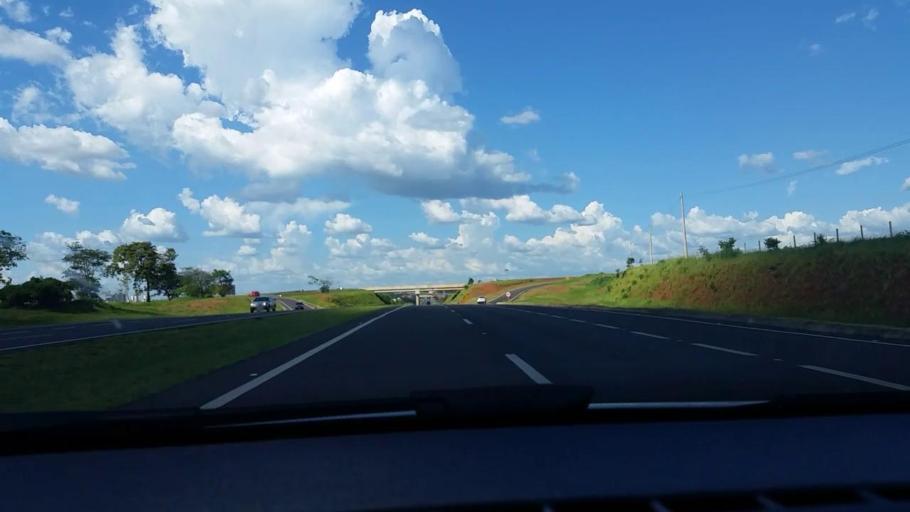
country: BR
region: Sao Paulo
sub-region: Bauru
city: Bauru
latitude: -22.3793
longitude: -49.0630
